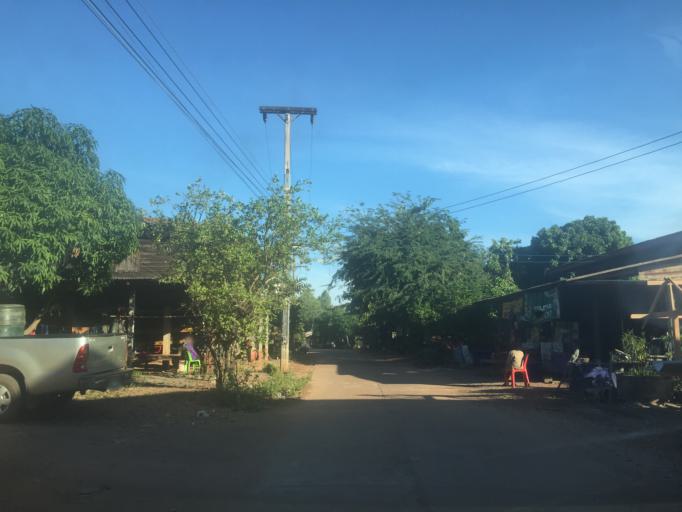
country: TH
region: Changwat Udon Thani
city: Si That
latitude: 16.9688
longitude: 103.2302
